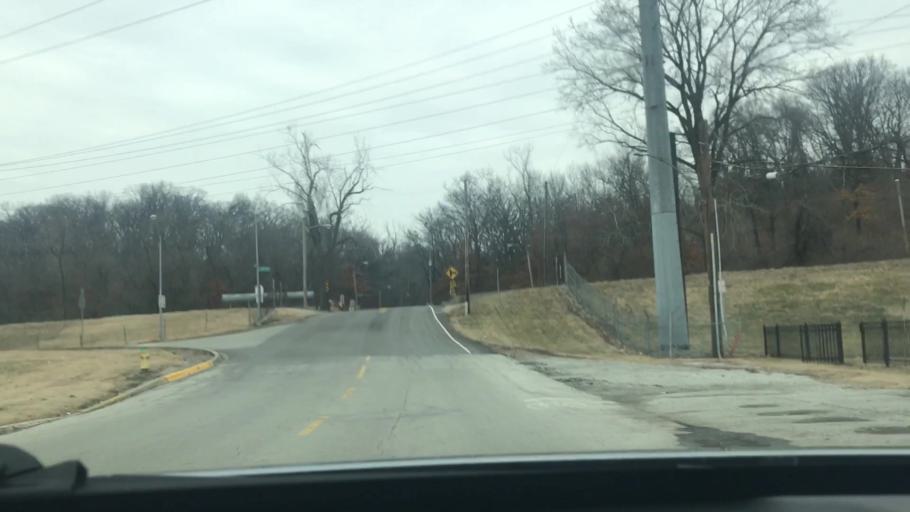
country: US
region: Missouri
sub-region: Clay County
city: North Kansas City
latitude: 39.1516
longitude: -94.5726
